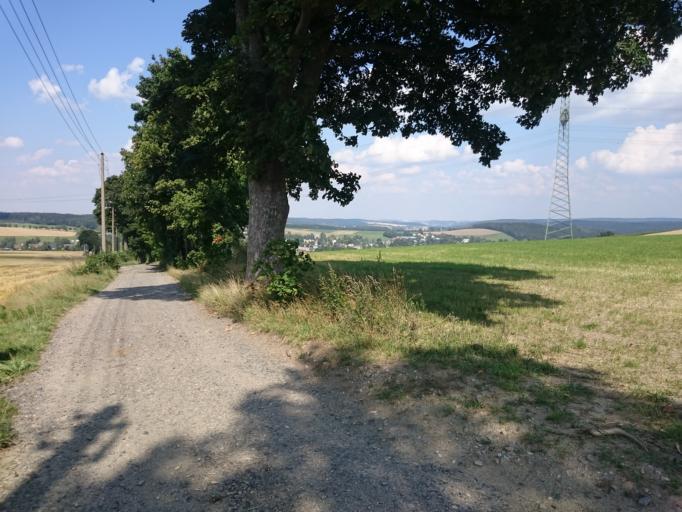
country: DE
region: Saxony
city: Dorfchemnitz
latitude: 50.6766
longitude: 12.8062
